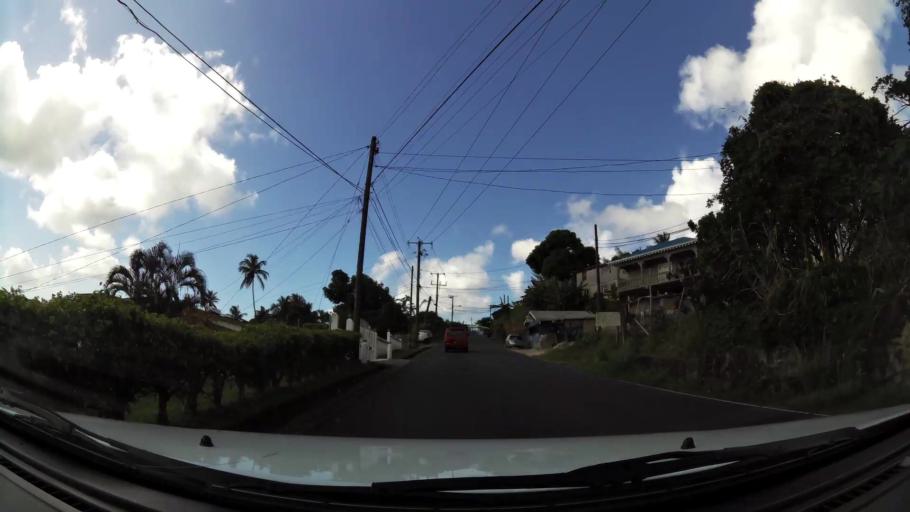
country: LC
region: Castries Quarter
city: Castries
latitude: 13.9977
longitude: -60.9999
